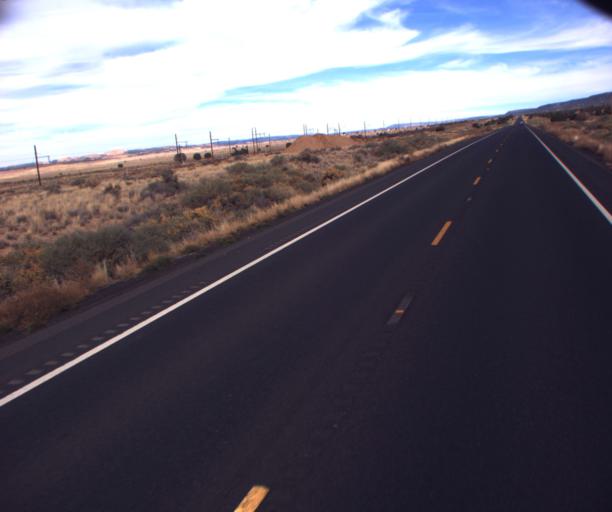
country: US
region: Arizona
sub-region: Coconino County
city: Kaibito
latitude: 36.4671
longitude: -110.6779
